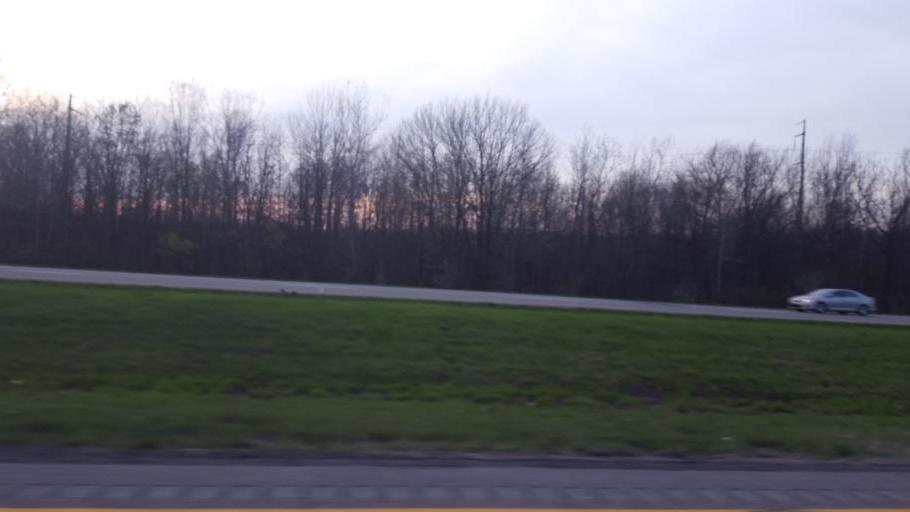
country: US
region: Ohio
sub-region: Lorain County
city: Sheffield
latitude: 41.4360
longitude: -82.0809
